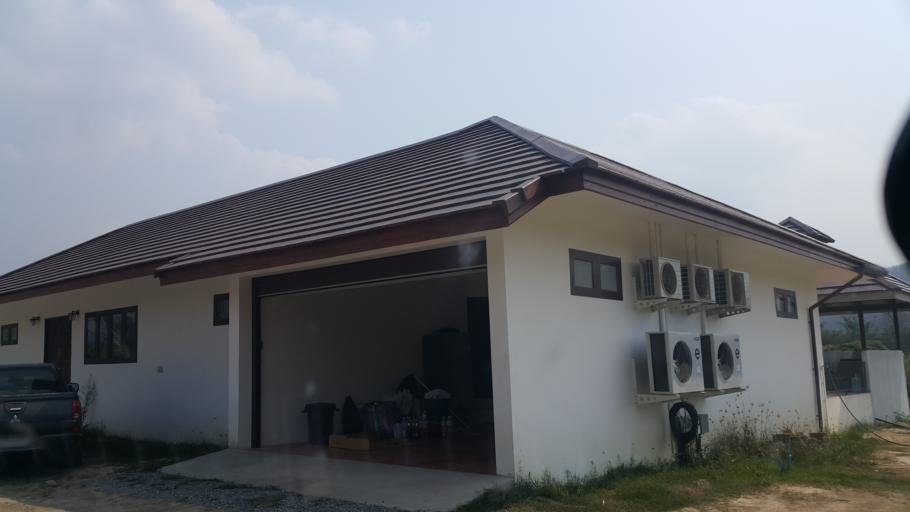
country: TH
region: Lamphun
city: Ban Thi
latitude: 18.6266
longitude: 99.1597
